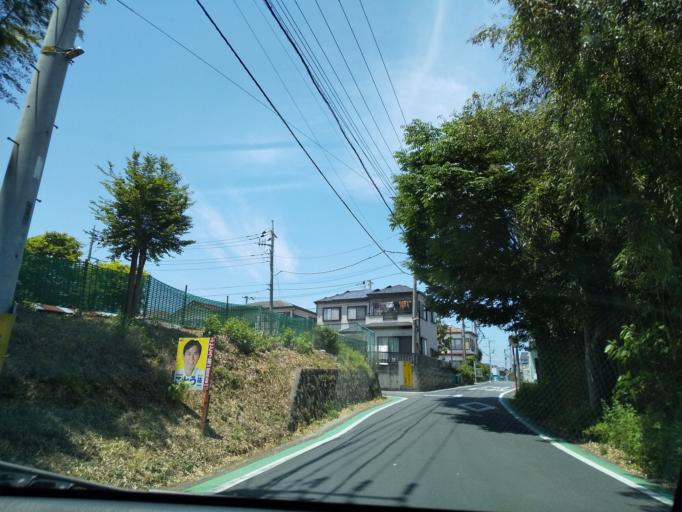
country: JP
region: Kanagawa
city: Zama
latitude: 35.5242
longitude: 139.3817
